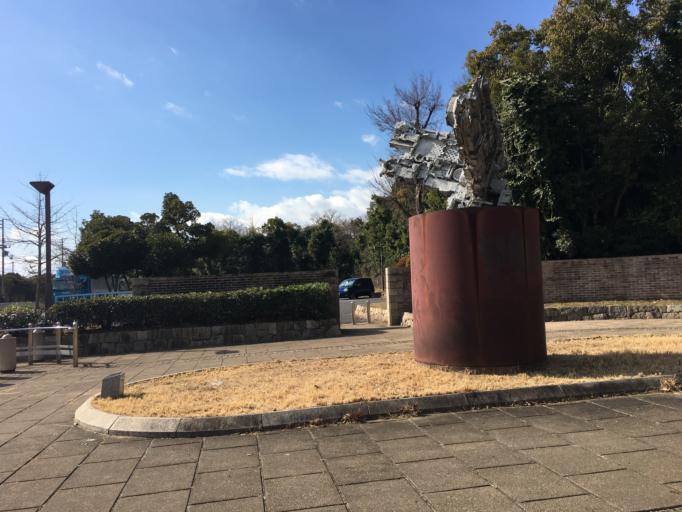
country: JP
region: Hyogo
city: Amagasaki
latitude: 34.6359
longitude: 135.4028
